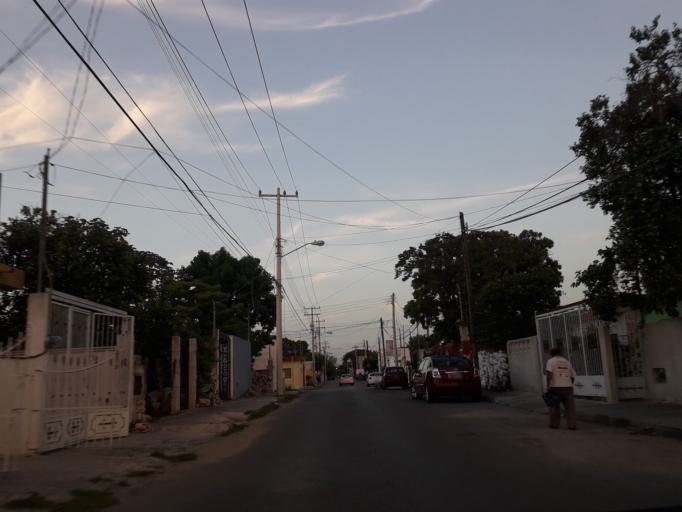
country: MX
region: Yucatan
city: Merida
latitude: 20.9856
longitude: -89.6539
